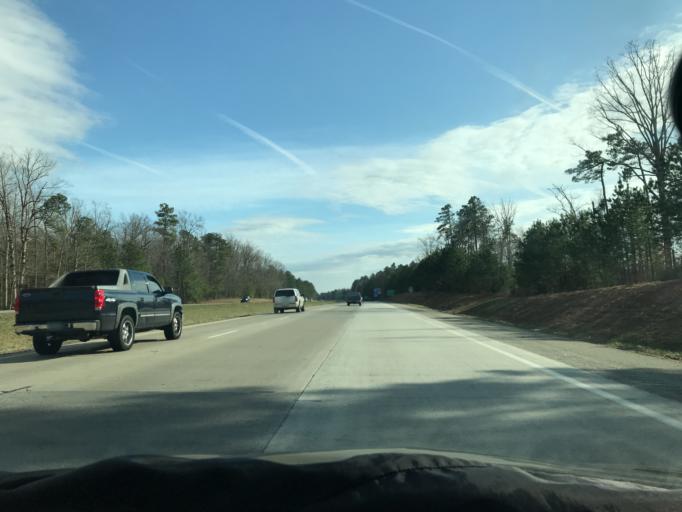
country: US
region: Virginia
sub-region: Chesterfield County
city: Brandermill
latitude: 37.4486
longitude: -77.6373
